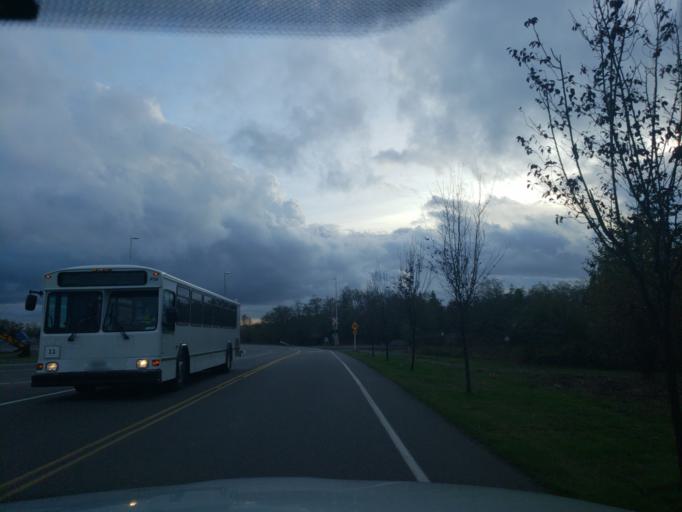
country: US
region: Washington
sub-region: Snohomish County
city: Mukilteo
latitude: 47.9284
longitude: -122.2848
